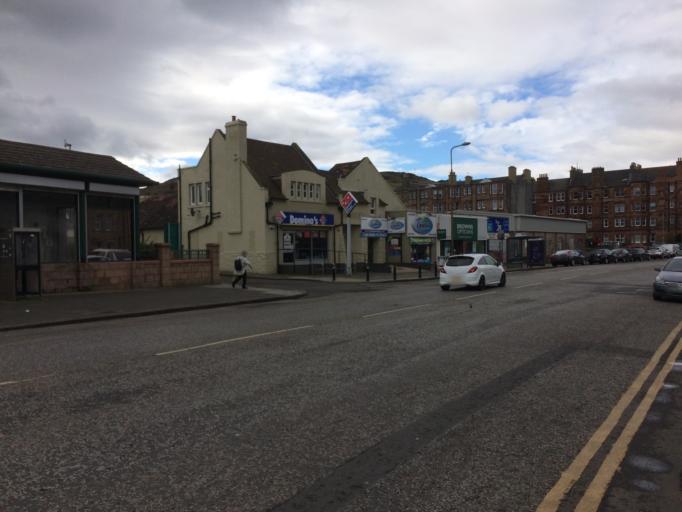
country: GB
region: Scotland
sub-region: West Lothian
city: Seafield
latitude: 55.9552
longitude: -3.1440
